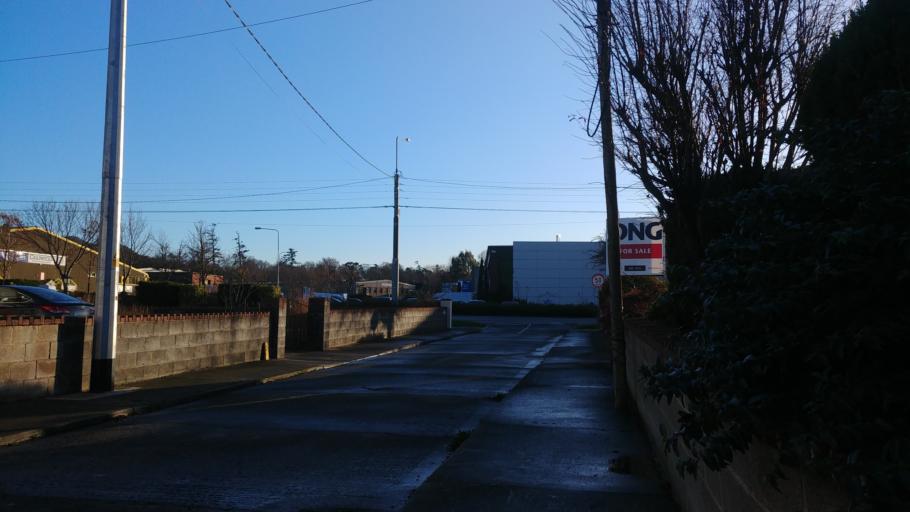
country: IE
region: Leinster
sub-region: Wicklow
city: Bray
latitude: 53.1889
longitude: -6.1054
